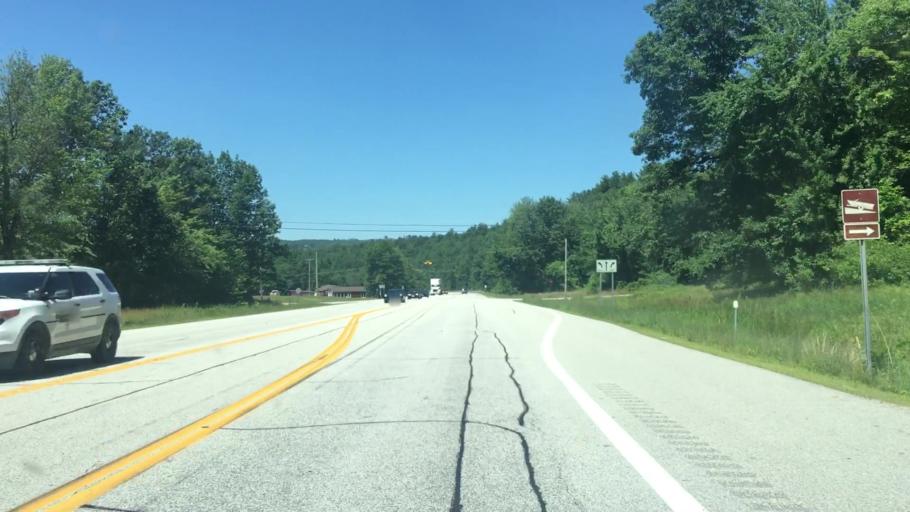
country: US
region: New Hampshire
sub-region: Merrimack County
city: Henniker
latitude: 43.1843
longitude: -71.7868
